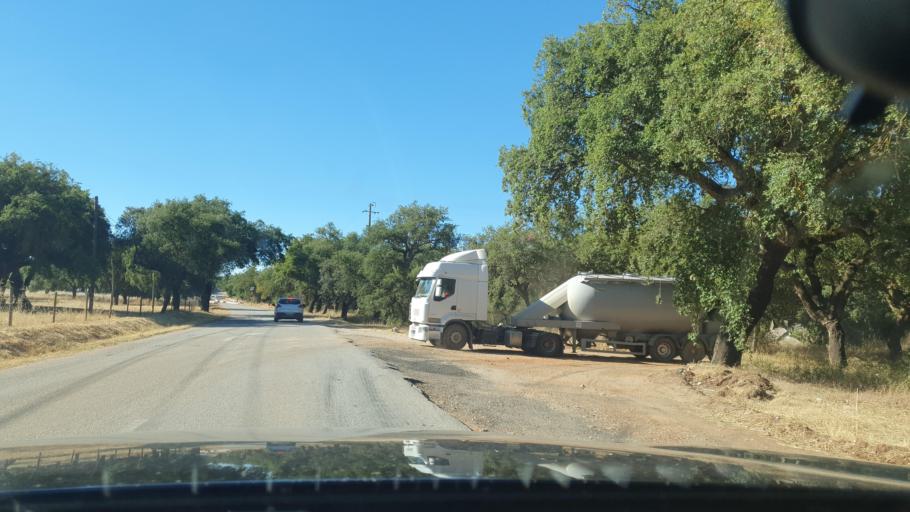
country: PT
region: Evora
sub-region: Alandroal
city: Alandroal
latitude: 38.7384
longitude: -7.4040
